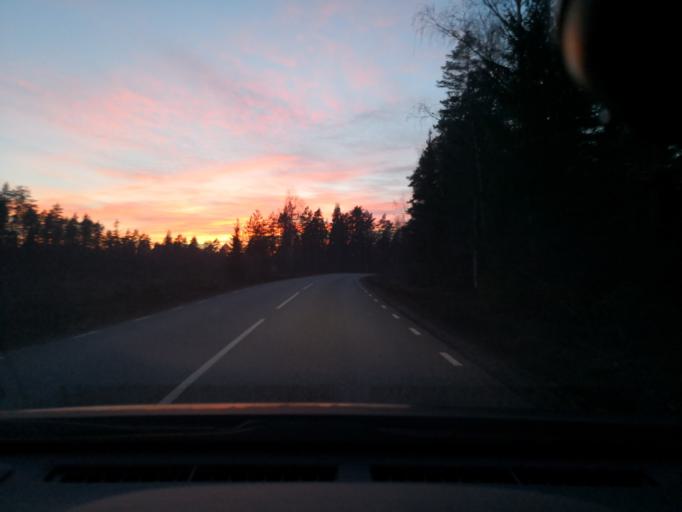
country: SE
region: OErebro
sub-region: Lindesbergs Kommun
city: Fellingsbro
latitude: 59.4030
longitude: 15.4935
